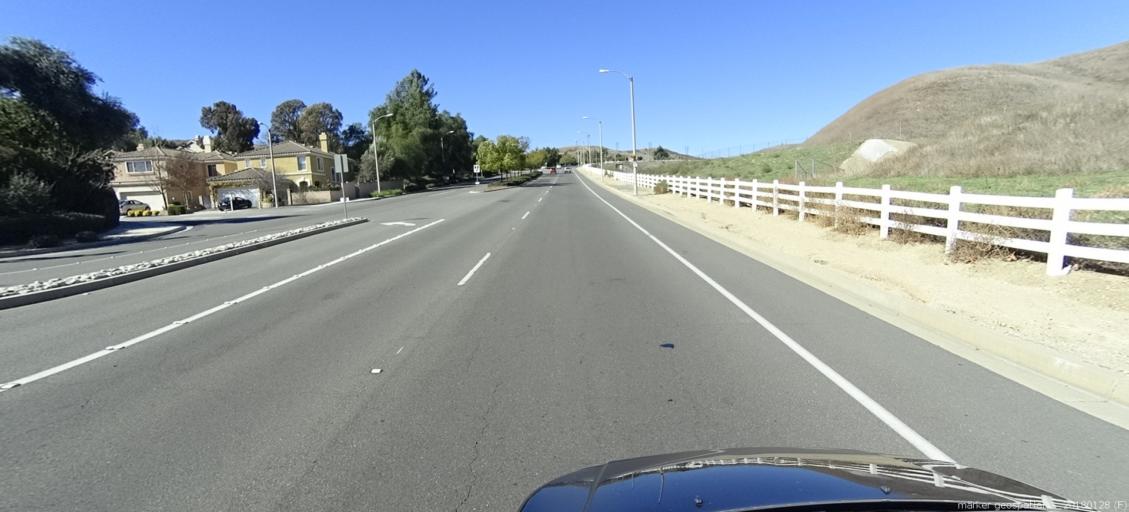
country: US
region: California
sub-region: San Bernardino County
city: Chino Hills
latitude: 33.9981
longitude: -117.7620
